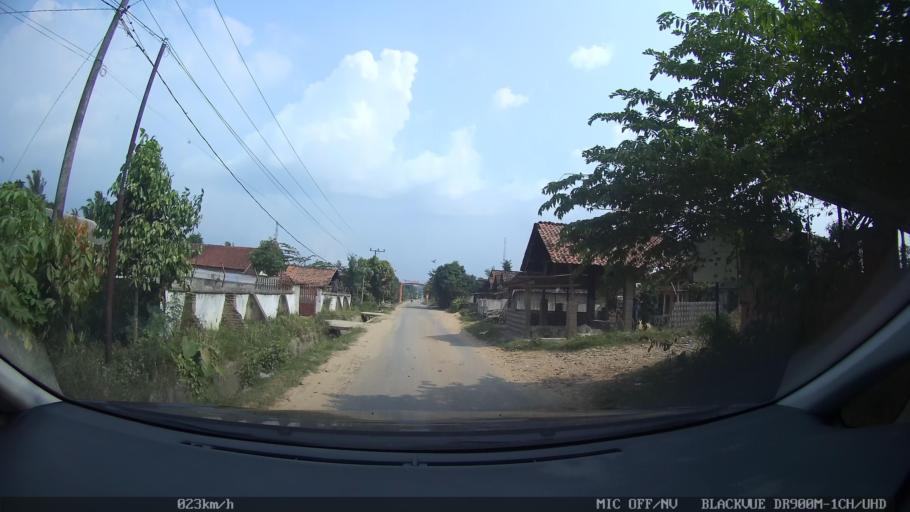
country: ID
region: Lampung
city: Pringsewu
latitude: -5.4064
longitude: 104.9922
